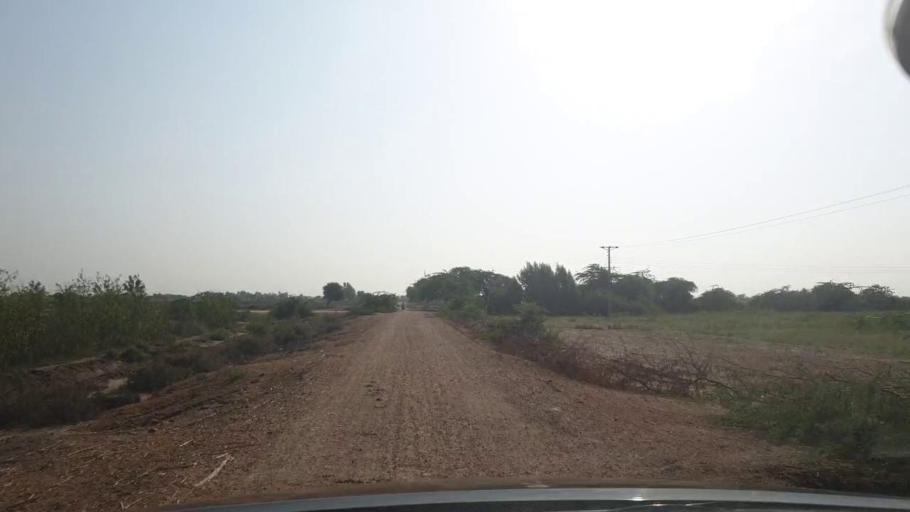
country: PK
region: Sindh
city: Tando Bago
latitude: 24.6510
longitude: 69.1526
